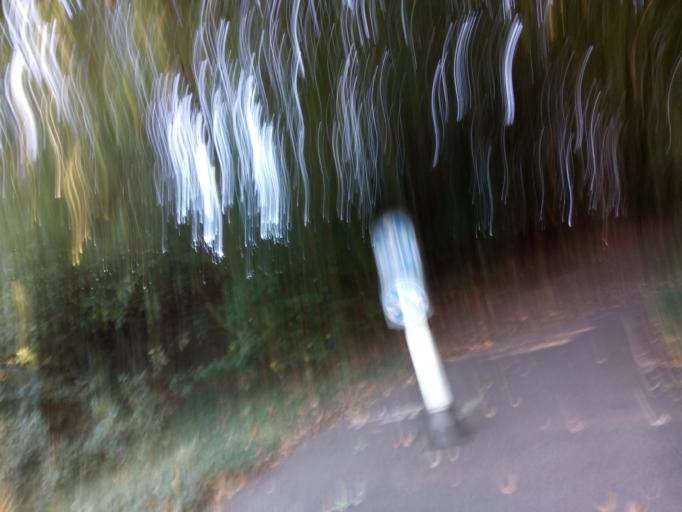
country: GB
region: England
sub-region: Suffolk
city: Bramford
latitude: 52.0408
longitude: 1.0972
